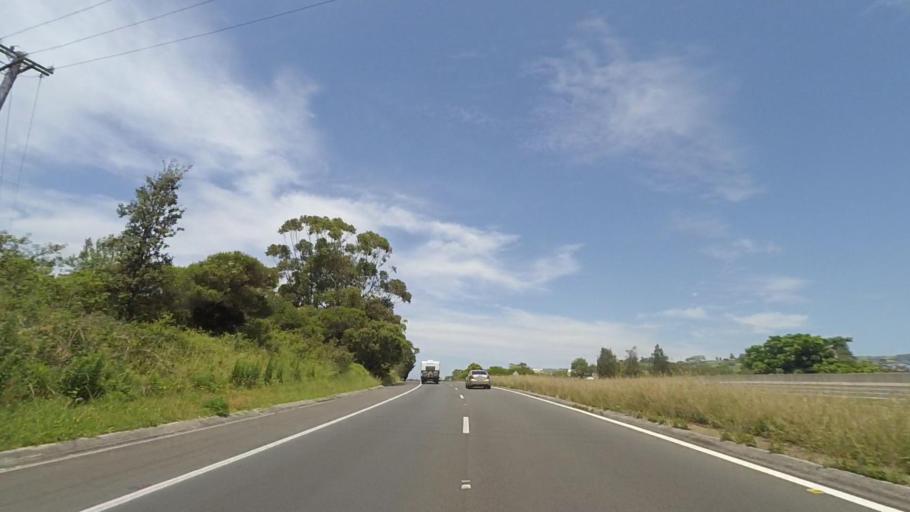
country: AU
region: New South Wales
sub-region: Kiama
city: Kiama
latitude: -34.6734
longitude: 150.8428
